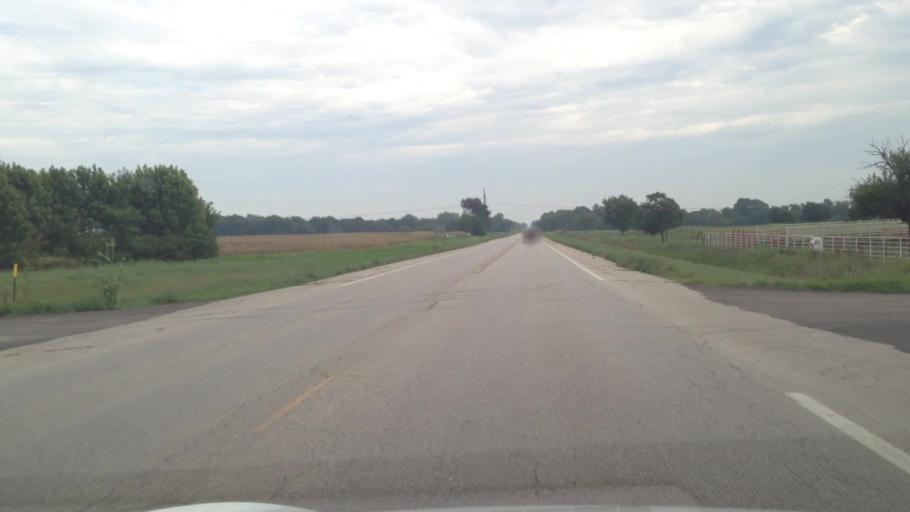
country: US
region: Kansas
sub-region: Crawford County
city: Pittsburg
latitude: 37.3393
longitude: -94.7963
